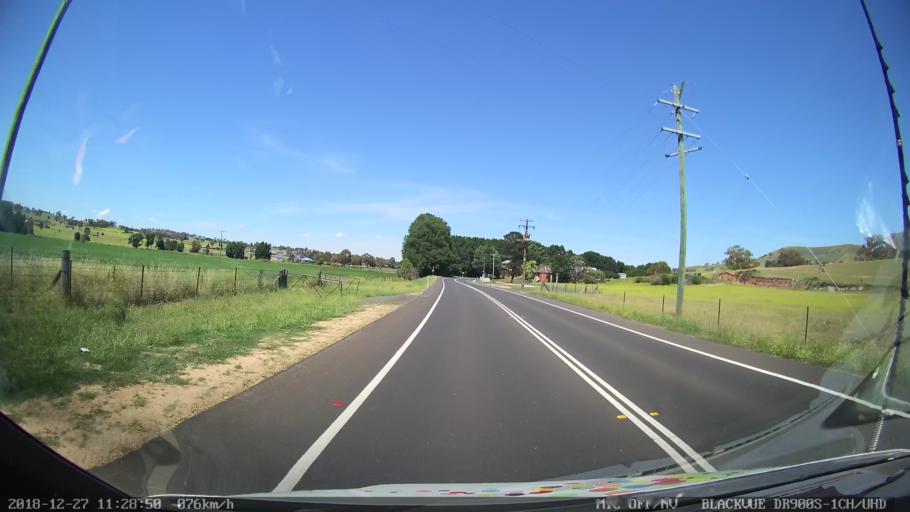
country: AU
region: New South Wales
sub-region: Bathurst Regional
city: Perthville
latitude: -33.4810
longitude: 149.5595
